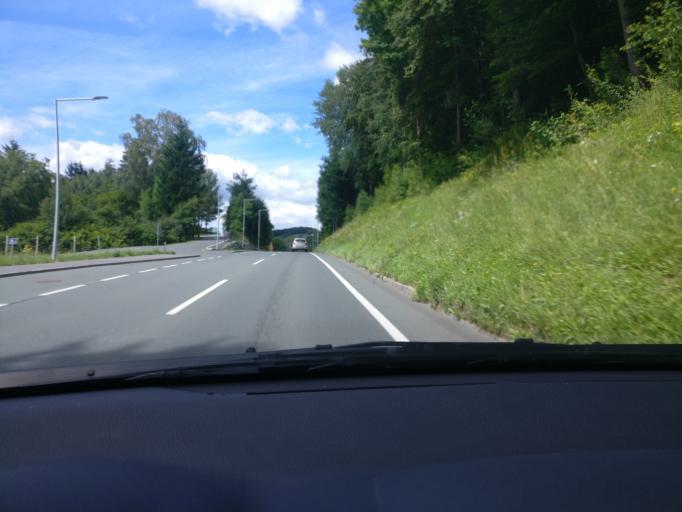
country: AT
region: Styria
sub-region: Politischer Bezirk Weiz
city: Hirnsdorf
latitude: 47.1852
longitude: 15.8144
